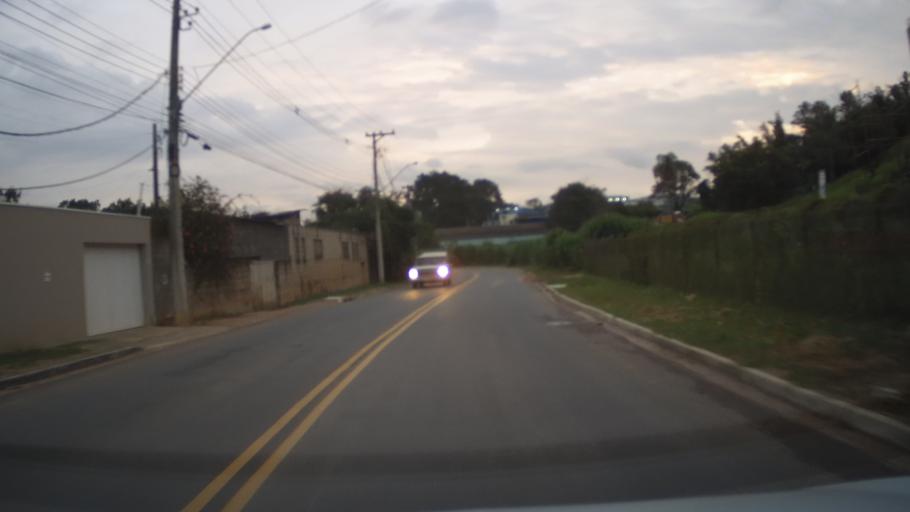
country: BR
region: Sao Paulo
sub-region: Vinhedo
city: Vinhedo
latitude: -23.0566
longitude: -47.0088
